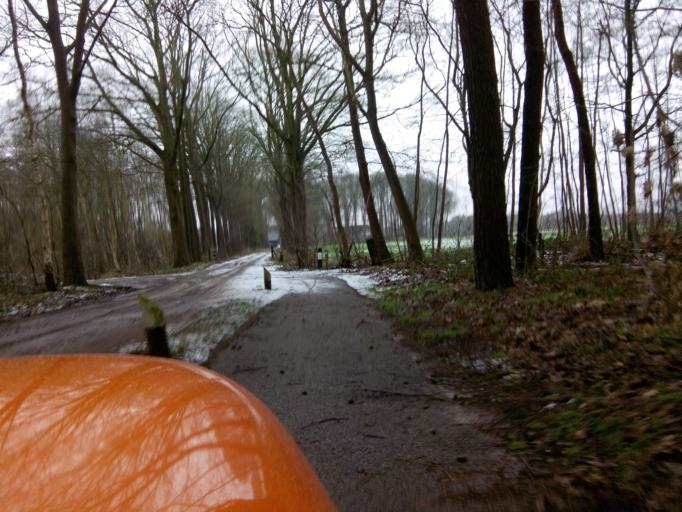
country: NL
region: Gelderland
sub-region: Gemeente Putten
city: Putten
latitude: 52.2296
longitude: 5.5598
